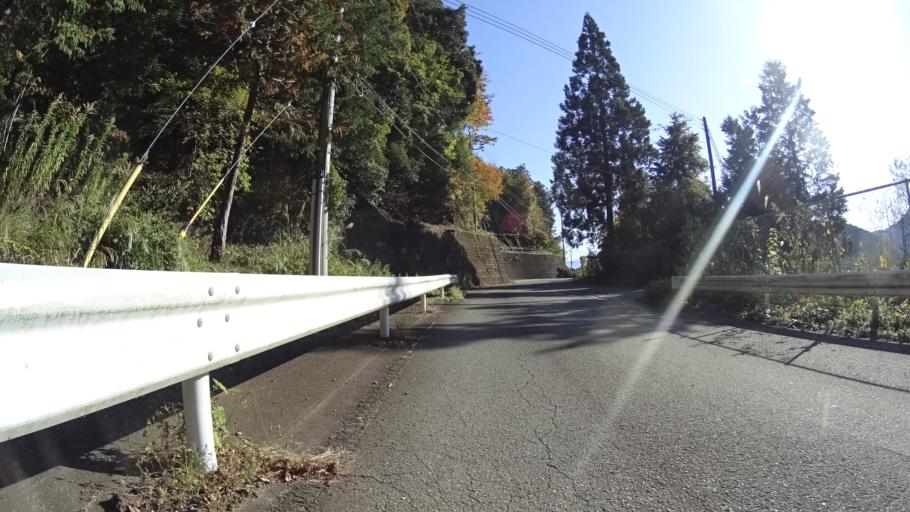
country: JP
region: Yamanashi
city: Uenohara
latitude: 35.6697
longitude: 139.1010
